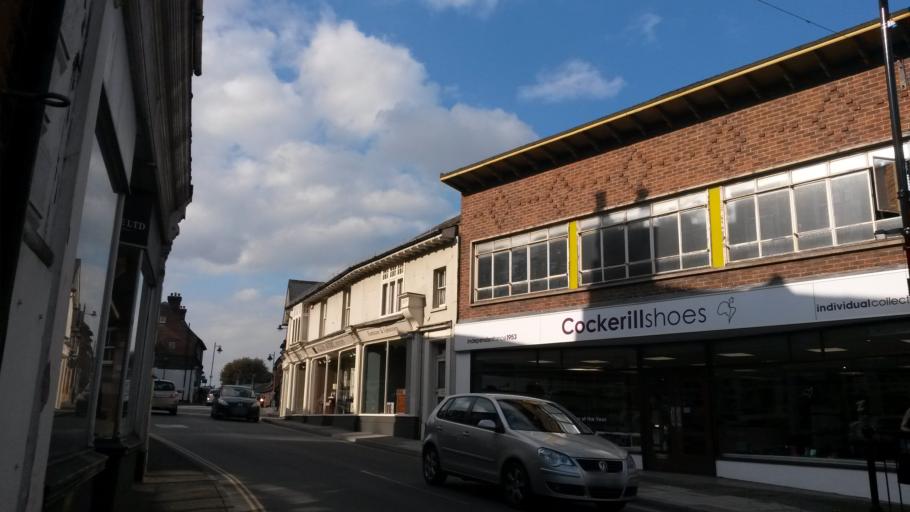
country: GB
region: England
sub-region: Surrey
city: Haslemere
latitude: 51.0876
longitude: -0.7099
